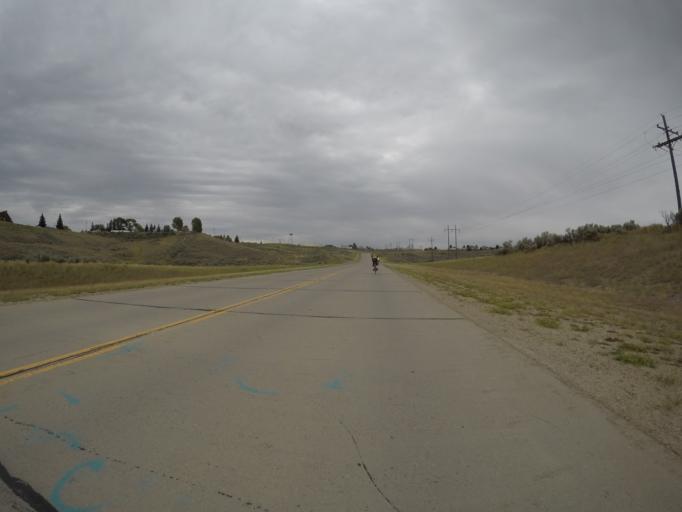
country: US
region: Wyoming
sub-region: Lincoln County
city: Kemmerer
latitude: 41.7968
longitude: -110.5477
